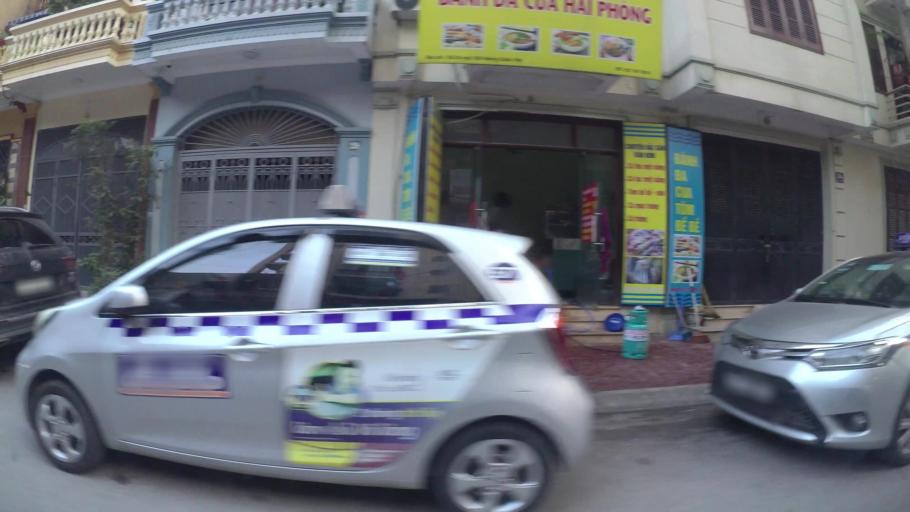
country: VN
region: Ha Noi
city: Cau Giay
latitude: 21.0484
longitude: 105.7950
